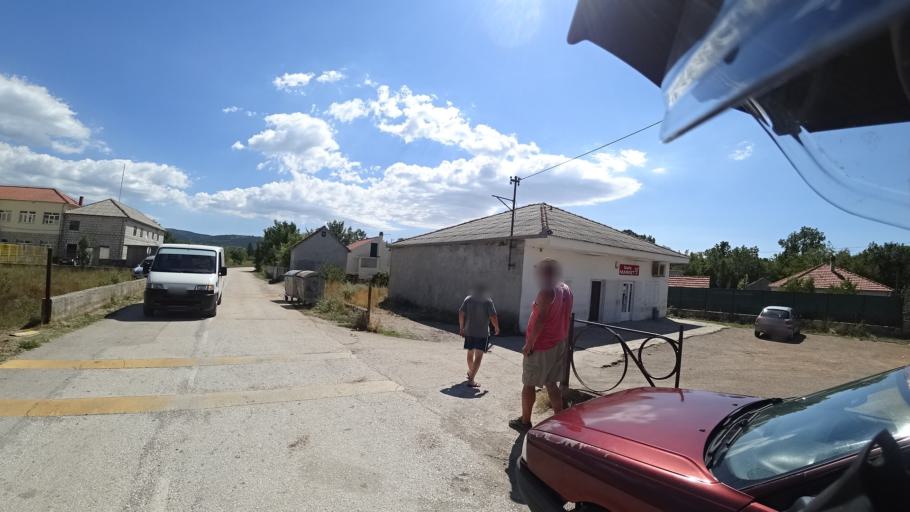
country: HR
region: Splitsko-Dalmatinska
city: Hrvace
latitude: 43.7419
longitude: 16.4377
